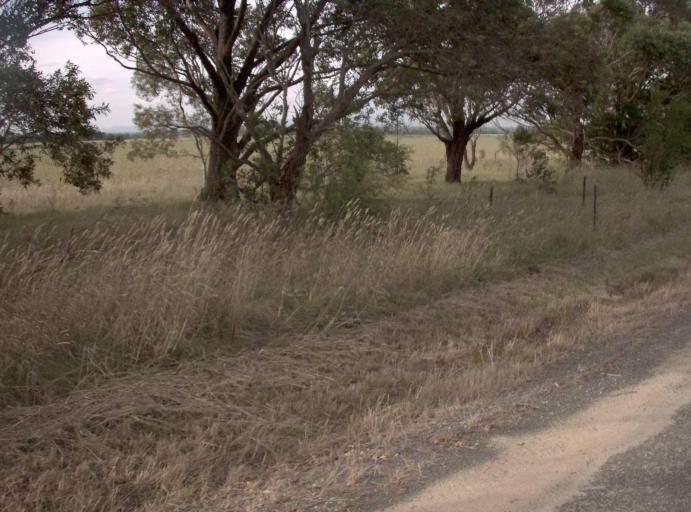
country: AU
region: Victoria
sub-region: Wellington
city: Heyfield
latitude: -38.0211
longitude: 146.7663
